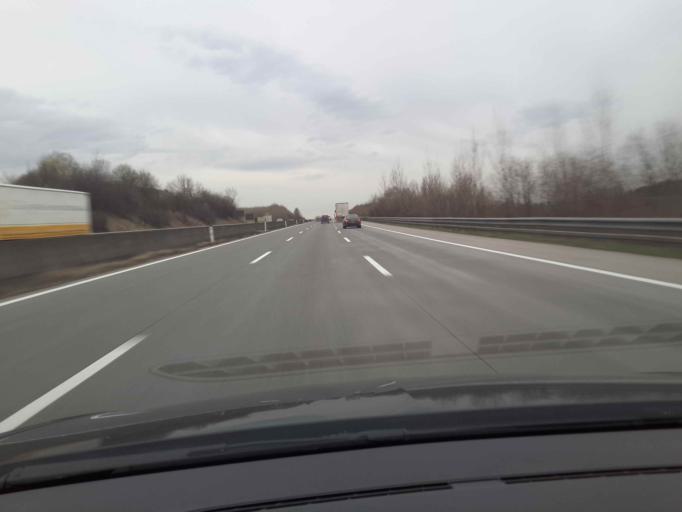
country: AT
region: Lower Austria
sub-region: Politischer Bezirk Amstetten
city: Zeillern
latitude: 48.1192
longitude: 14.7741
